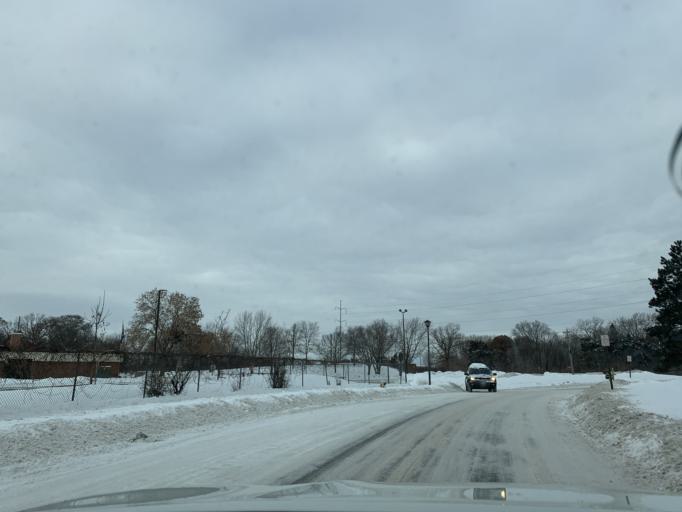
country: US
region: Minnesota
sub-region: Hennepin County
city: West Coon Rapids
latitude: 45.1705
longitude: -93.2999
